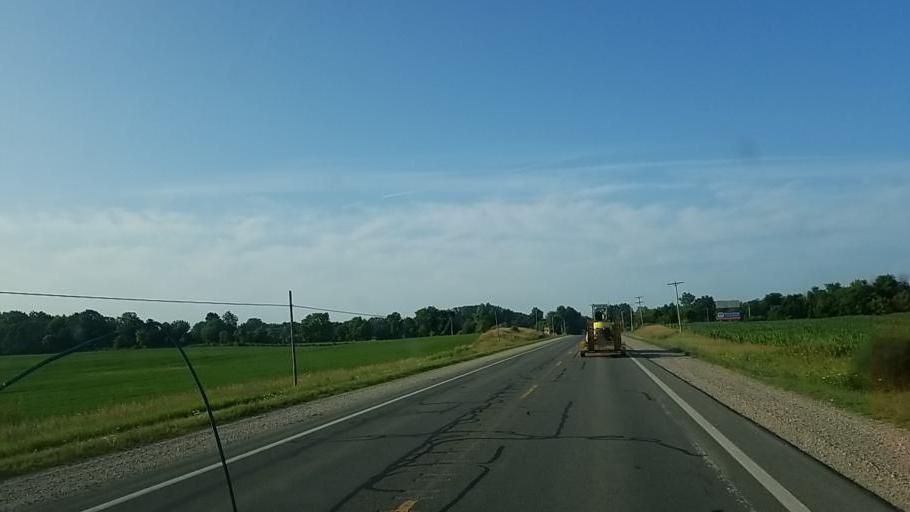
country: US
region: Michigan
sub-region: Montcalm County
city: Stanton
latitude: 43.1954
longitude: -85.0737
